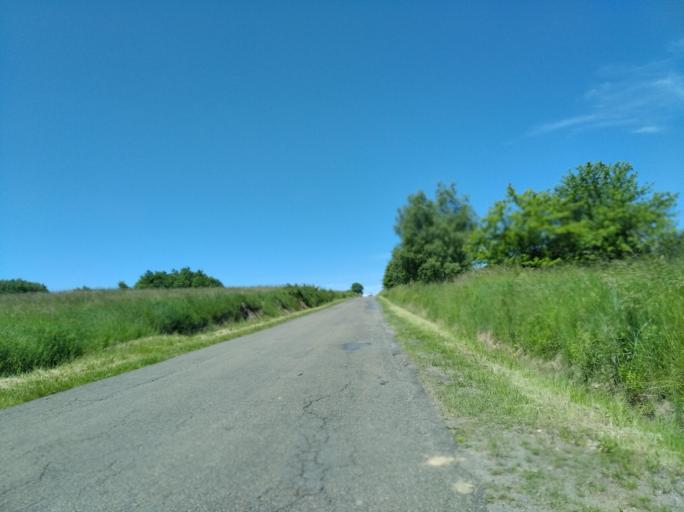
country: PL
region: Subcarpathian Voivodeship
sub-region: Powiat krosnienski
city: Chorkowka
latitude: 49.6409
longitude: 21.6281
